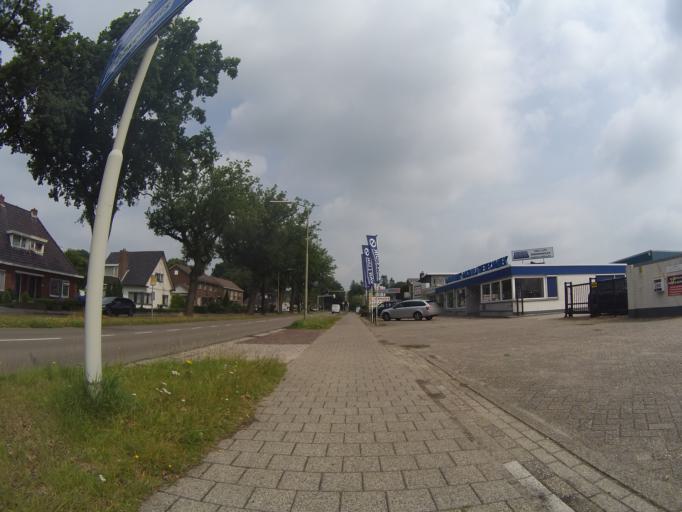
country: NL
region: Drenthe
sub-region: Gemeente Emmen
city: Emmen
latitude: 52.7981
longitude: 6.9010
